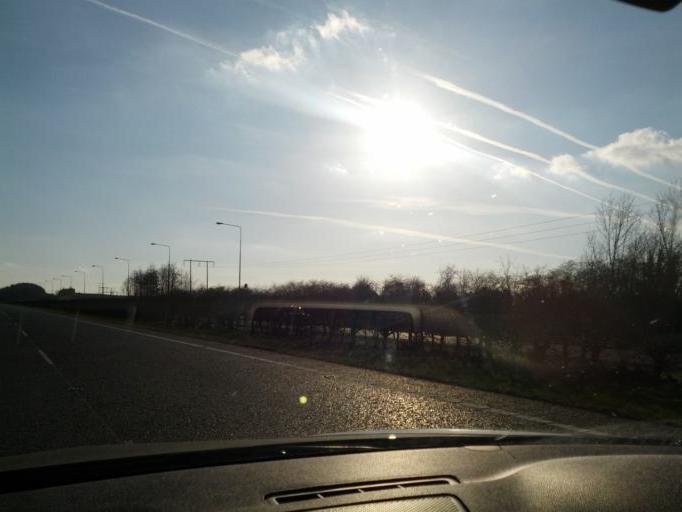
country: IE
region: Leinster
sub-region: Laois
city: Portlaoise
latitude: 53.0574
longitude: -7.2308
